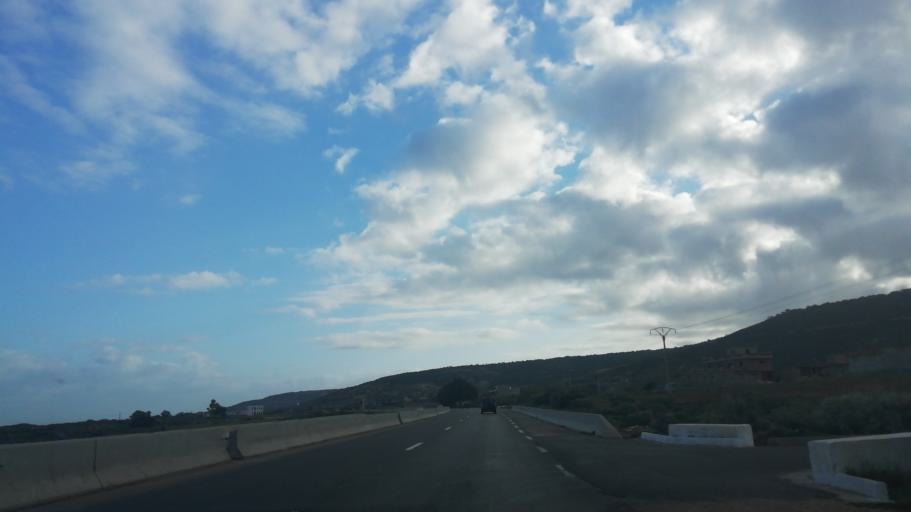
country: DZ
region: Mostaganem
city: Mostaganem
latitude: 36.0776
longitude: 0.1871
